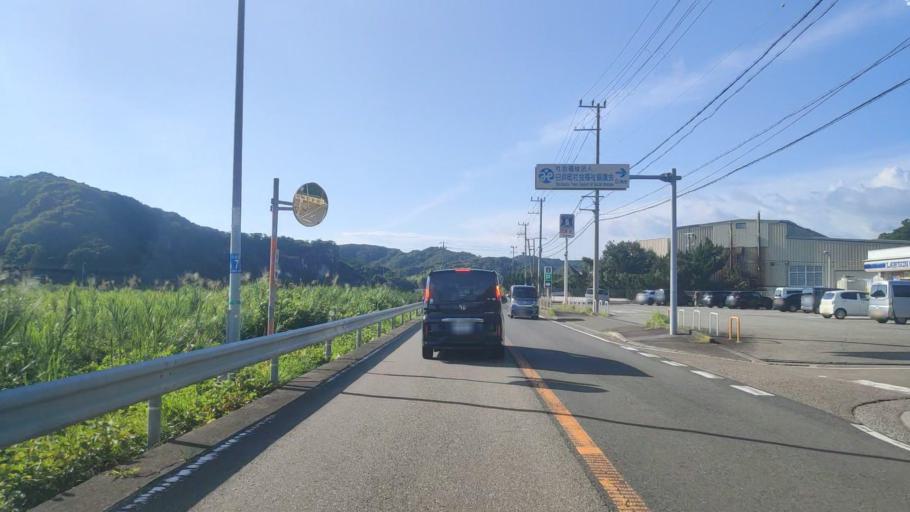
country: JP
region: Wakayama
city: Tanabe
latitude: 33.6594
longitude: 135.4000
